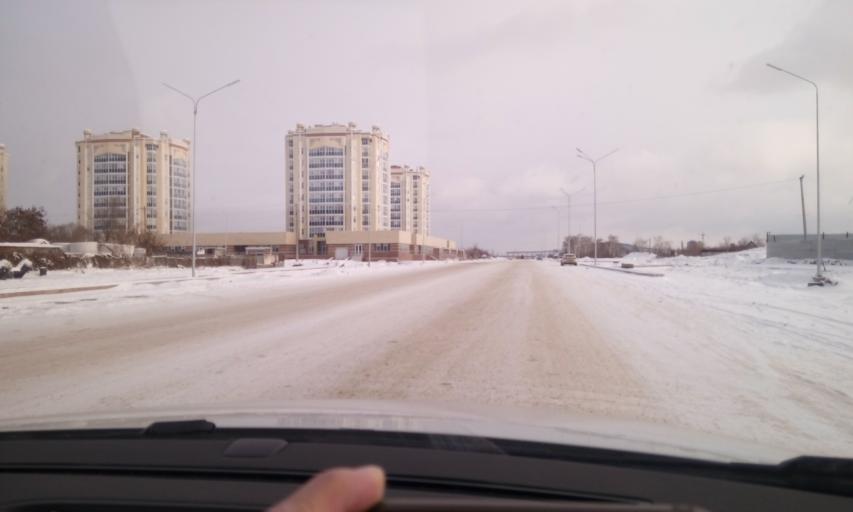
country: KZ
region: Astana Qalasy
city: Astana
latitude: 51.1196
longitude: 71.5012
